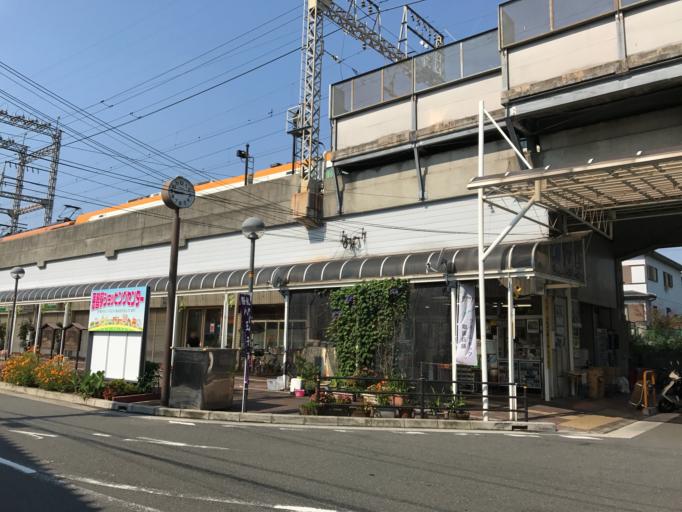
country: JP
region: Osaka
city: Yao
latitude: 34.6094
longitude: 135.6264
